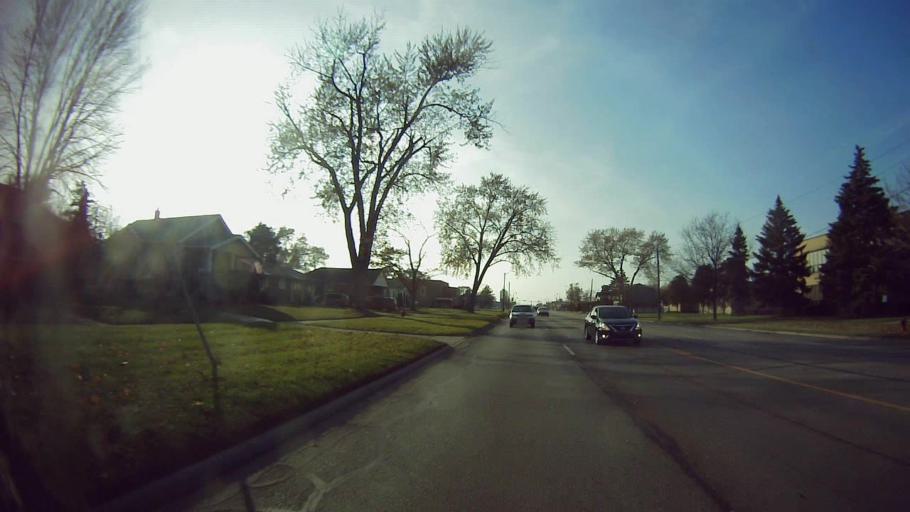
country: US
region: Michigan
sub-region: Oakland County
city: Clawson
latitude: 42.5336
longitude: -83.1389
